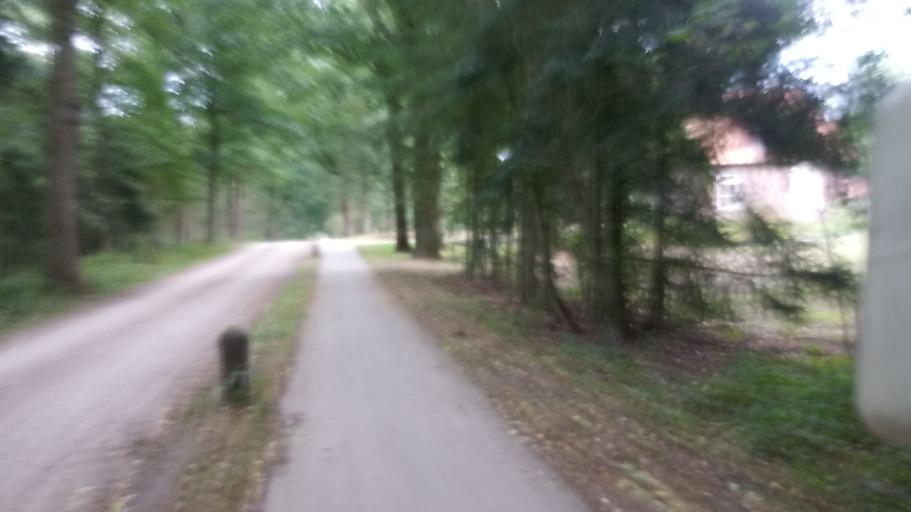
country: NL
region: Gelderland
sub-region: Gemeente Voorst
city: Voorst
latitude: 52.1743
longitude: 6.0863
